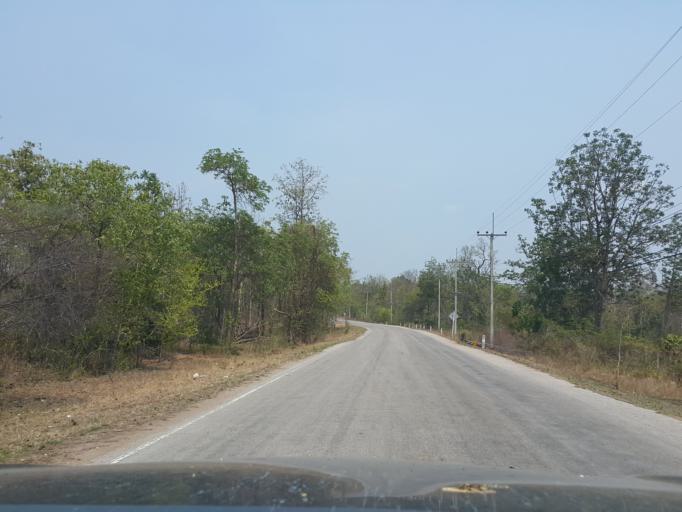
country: TH
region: Lampang
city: Mae Phrik
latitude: 17.5448
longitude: 99.1333
